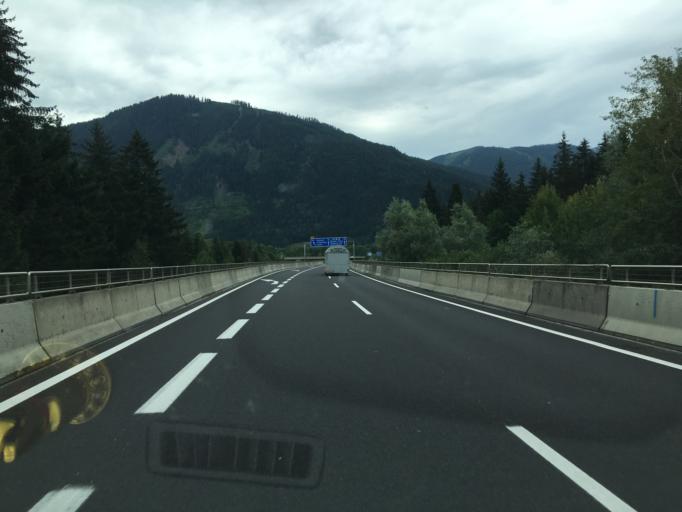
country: AT
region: Styria
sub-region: Politischer Bezirk Liezen
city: Selzthal
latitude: 47.5490
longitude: 14.3004
